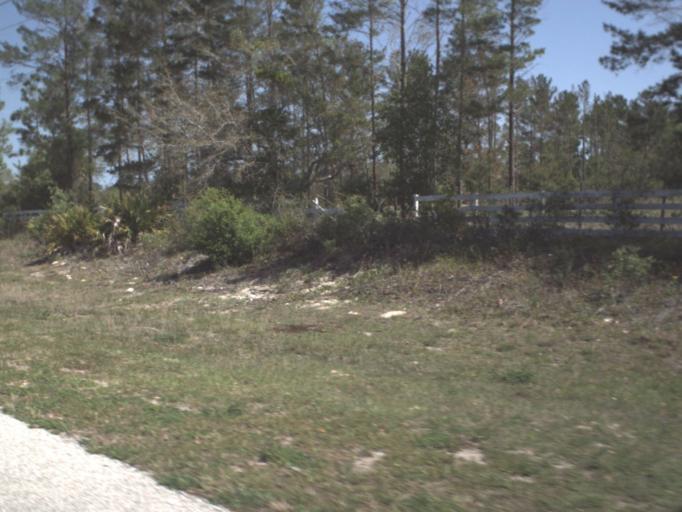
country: US
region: Florida
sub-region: Flagler County
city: Palm Coast
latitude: 29.6422
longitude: -81.2856
